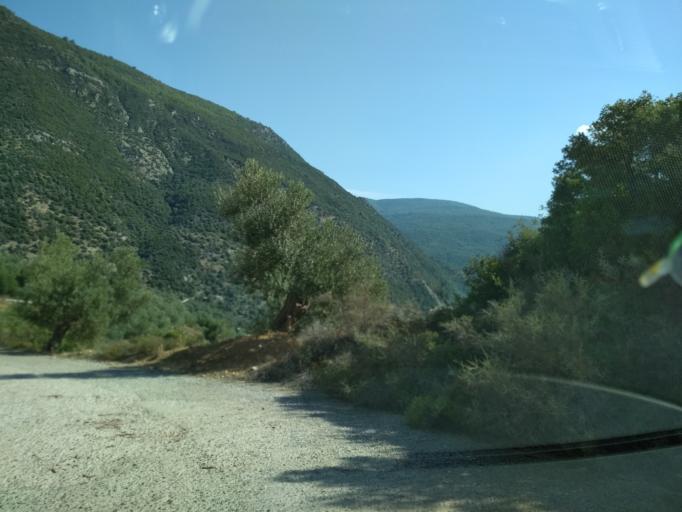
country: GR
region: Central Greece
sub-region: Nomos Evvoias
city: Oreoi
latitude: 38.8493
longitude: 23.1206
